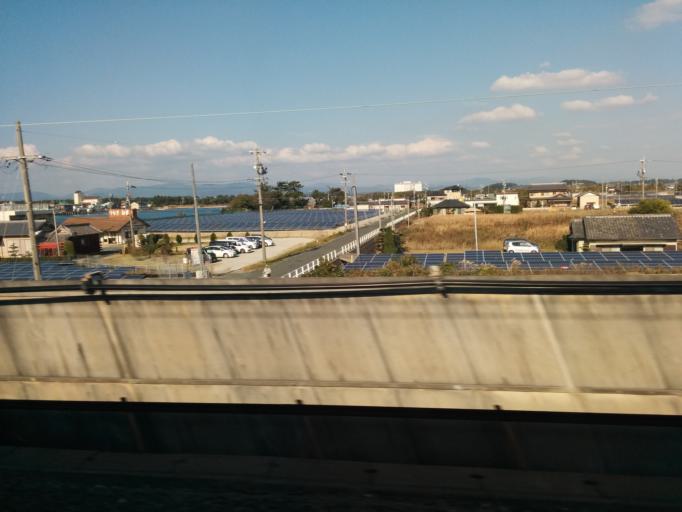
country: JP
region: Shizuoka
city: Kosai-shi
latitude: 34.6882
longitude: 137.6089
